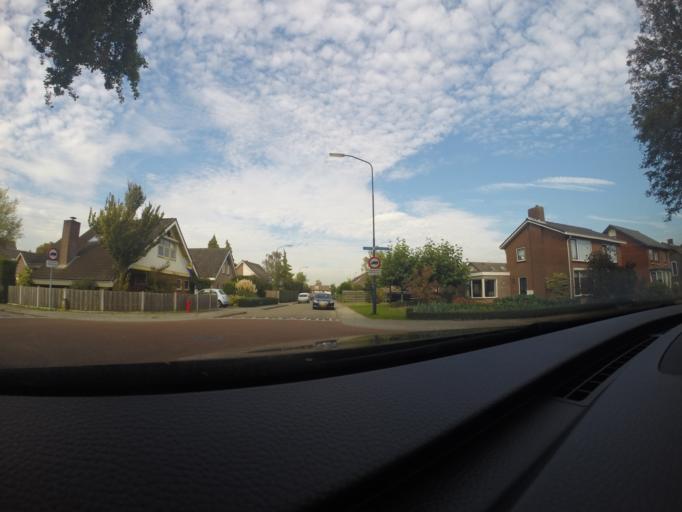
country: NL
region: Gelderland
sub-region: Gemeente Doetinchem
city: Doetinchem
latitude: 51.9621
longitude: 6.2154
